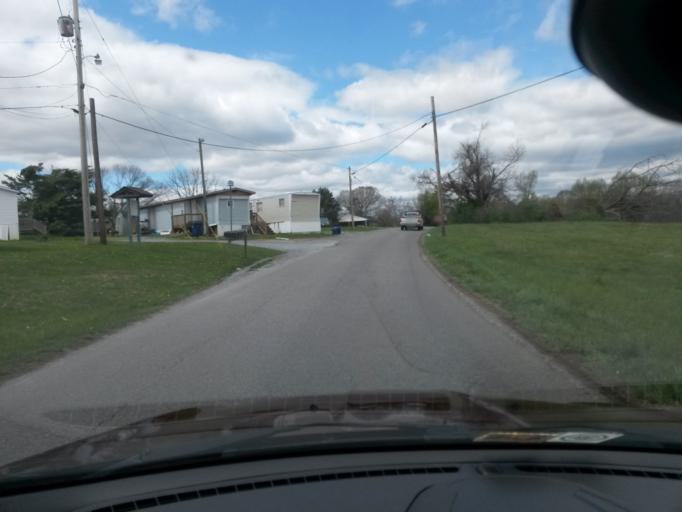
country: US
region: Virginia
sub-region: City of Lynchburg
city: West Lynchburg
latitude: 37.3978
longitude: -79.2126
